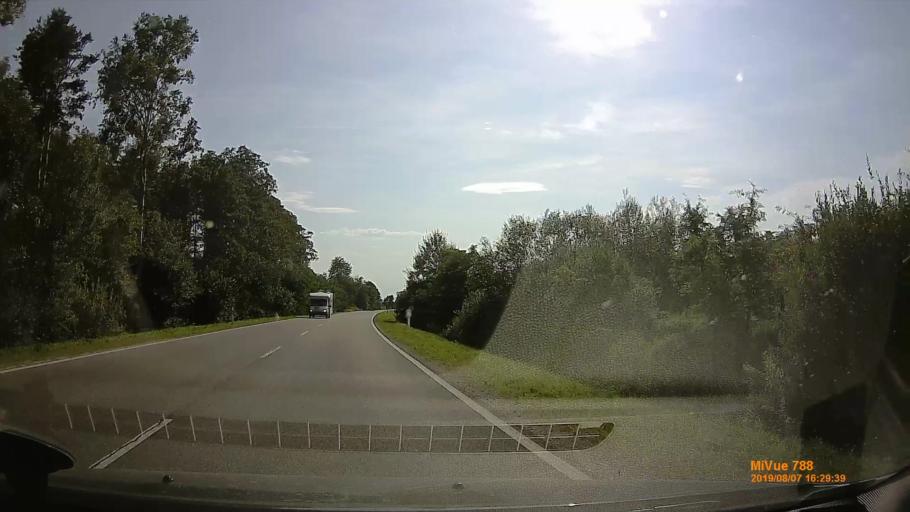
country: HU
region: Zala
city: Lenti
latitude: 46.6781
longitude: 16.5259
